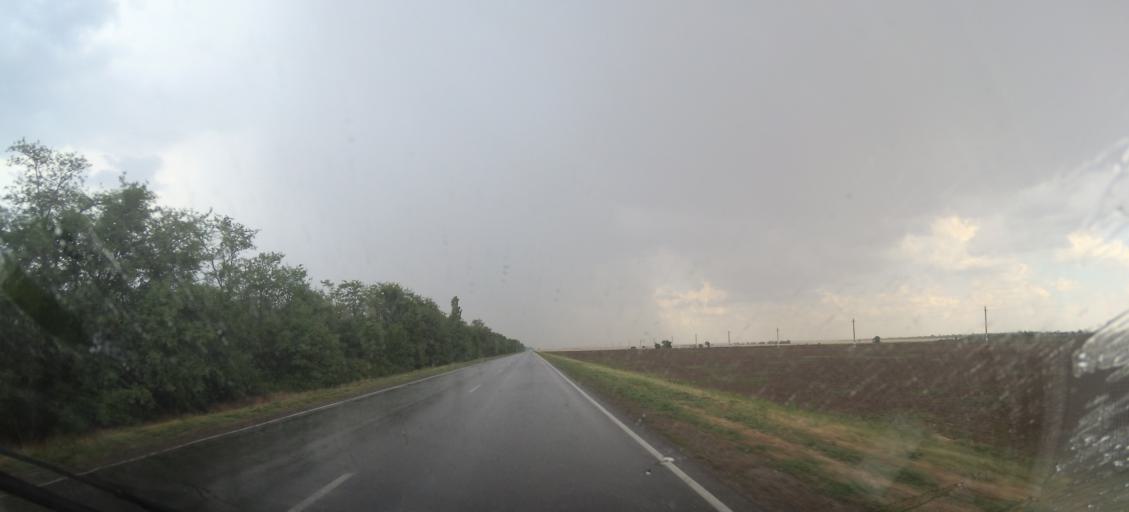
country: RU
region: Rostov
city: Proletarsk
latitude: 46.6577
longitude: 41.6830
